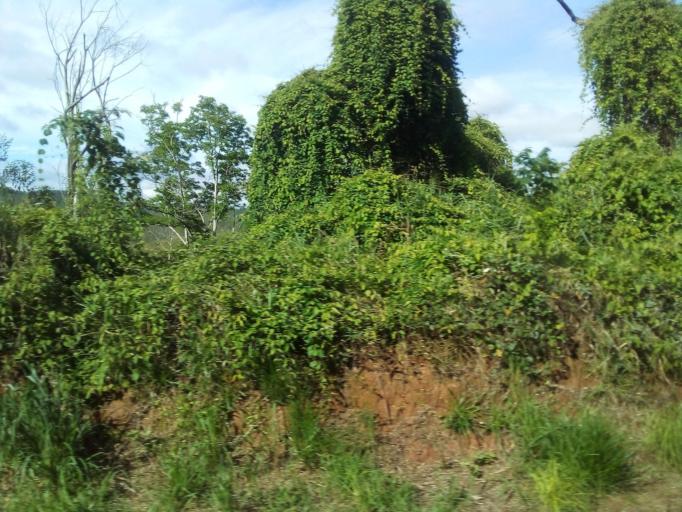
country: BR
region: Minas Gerais
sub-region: Caete
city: Caete
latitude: -19.8757
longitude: -43.7661
